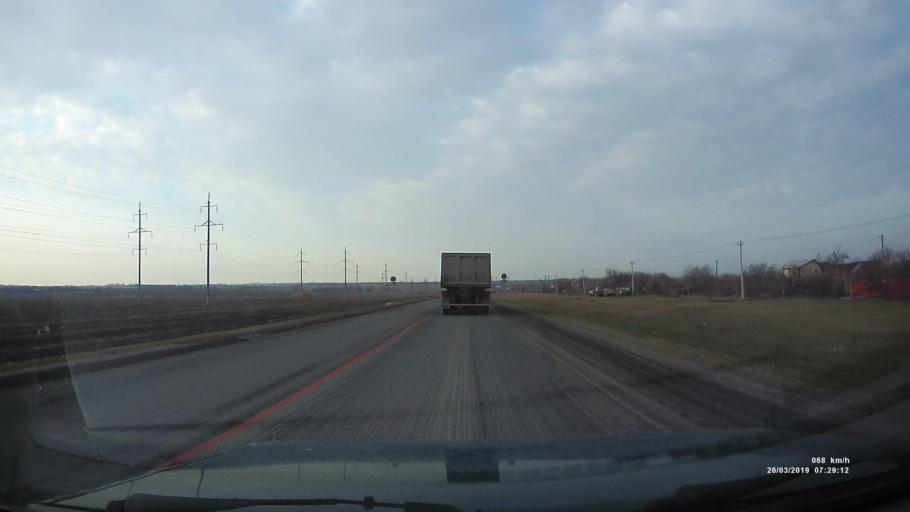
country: RU
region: Rostov
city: Novobessergenovka
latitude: 47.2474
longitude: 38.8185
